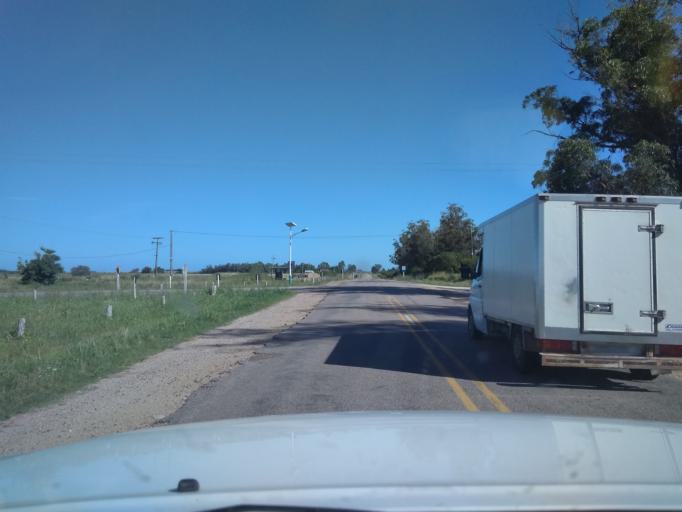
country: UY
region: Canelones
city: San Ramon
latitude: -34.2037
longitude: -55.9329
